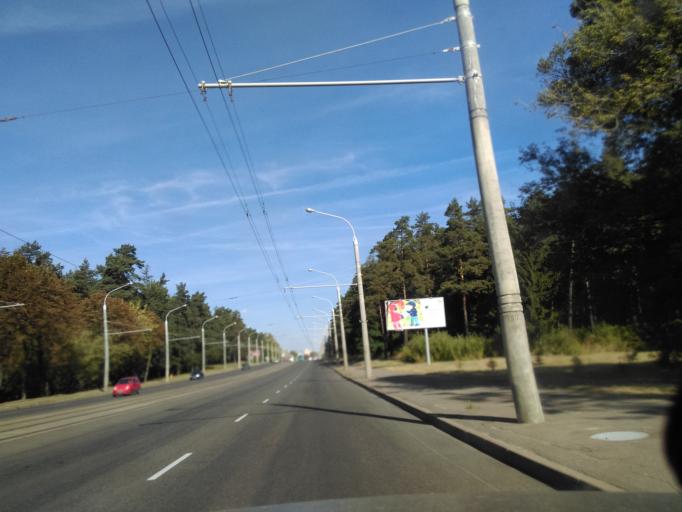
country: BY
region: Minsk
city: Minsk
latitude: 53.8798
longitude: 27.6256
